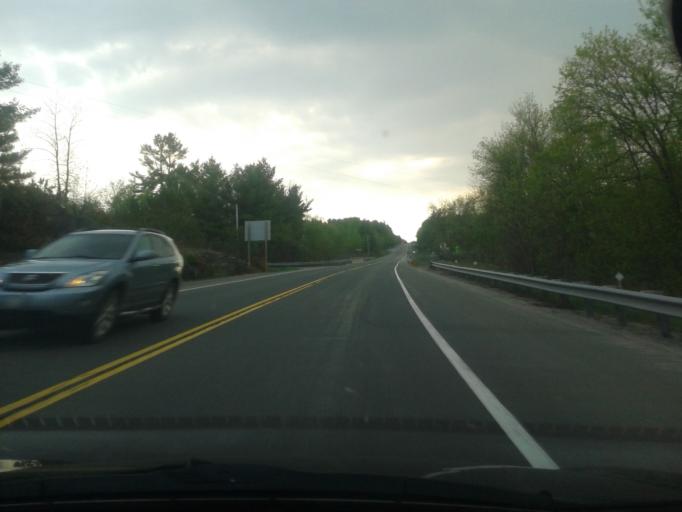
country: CA
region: Ontario
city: Belleville
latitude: 44.5497
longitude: -77.3271
